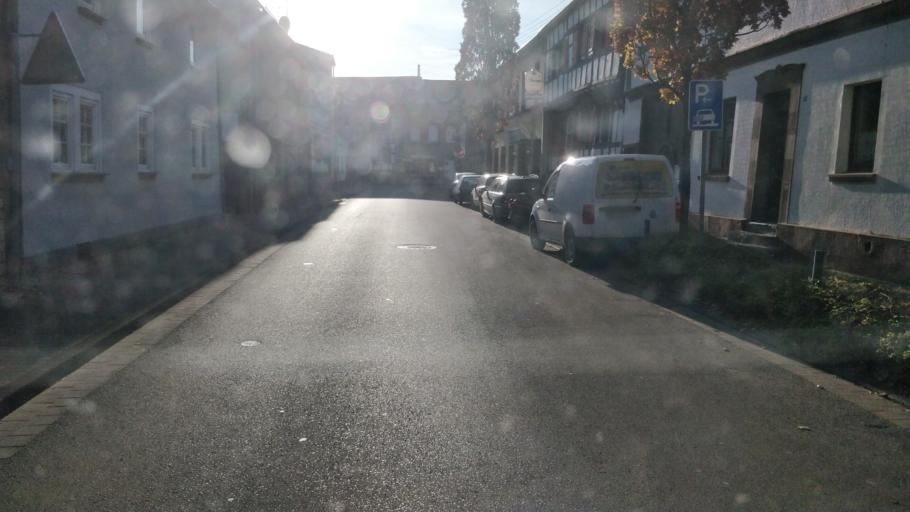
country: DE
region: North Rhine-Westphalia
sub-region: Regierungsbezirk Koln
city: Euskirchen
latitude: 50.6252
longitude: 6.8503
